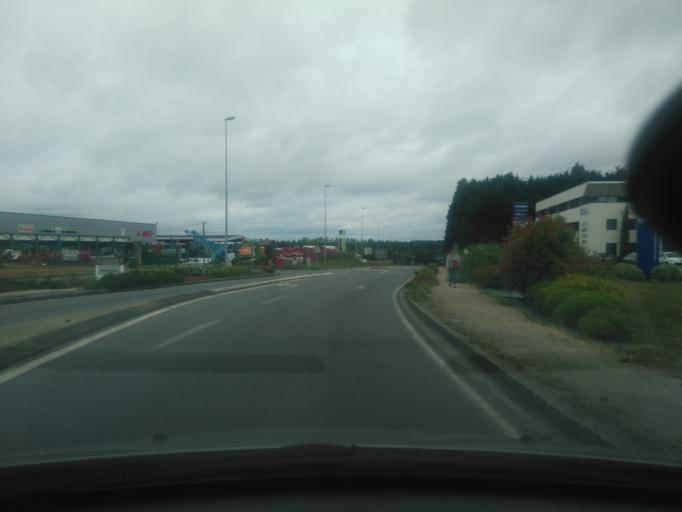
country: FR
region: Brittany
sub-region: Departement des Cotes-d'Armor
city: Lehon
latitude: 48.4655
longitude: -2.0589
